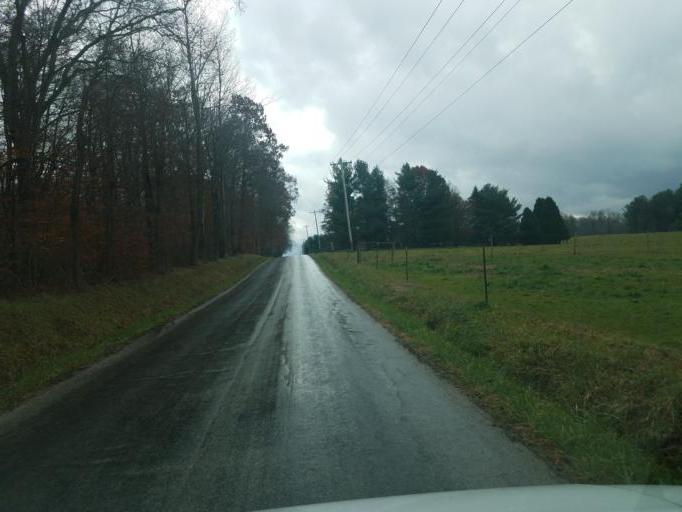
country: US
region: Ohio
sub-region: Richland County
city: Lexington
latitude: 40.6139
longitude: -82.6059
